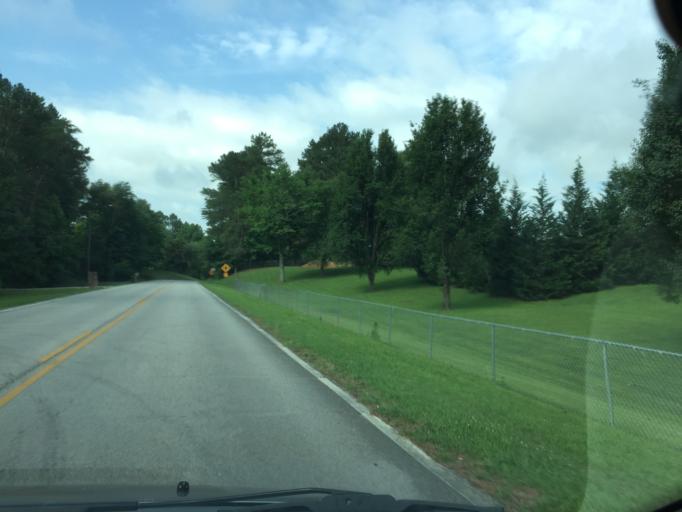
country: US
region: Tennessee
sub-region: Hamilton County
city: Apison
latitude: 35.0179
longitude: -85.0258
